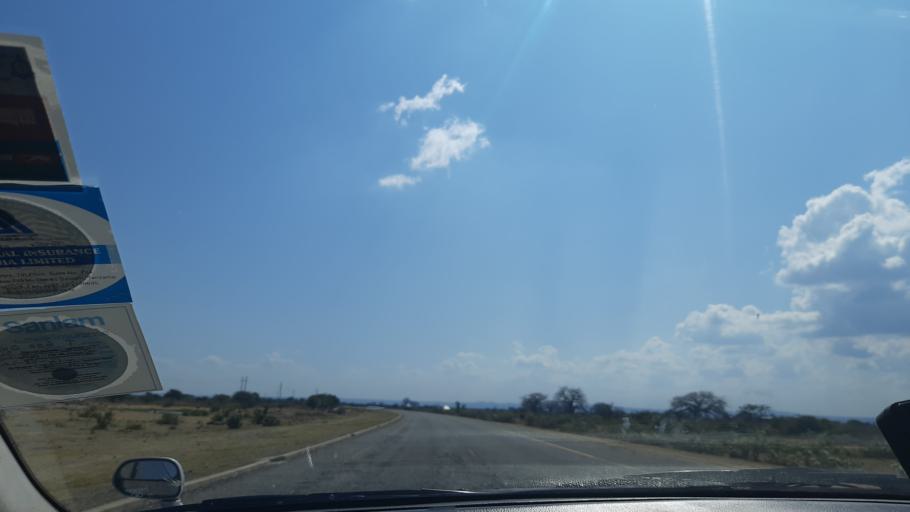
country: TZ
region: Singida
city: Kintinku
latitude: -5.8815
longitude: 35.1389
